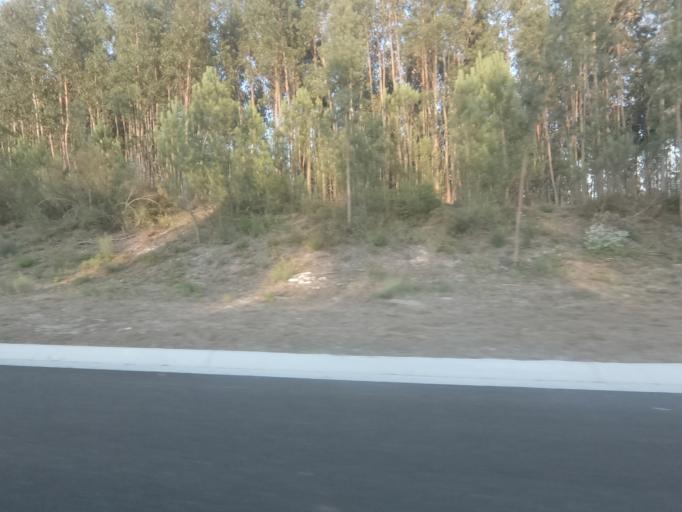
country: PT
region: Leiria
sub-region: Leiria
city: Caranguejeira
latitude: 39.7873
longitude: -8.7369
